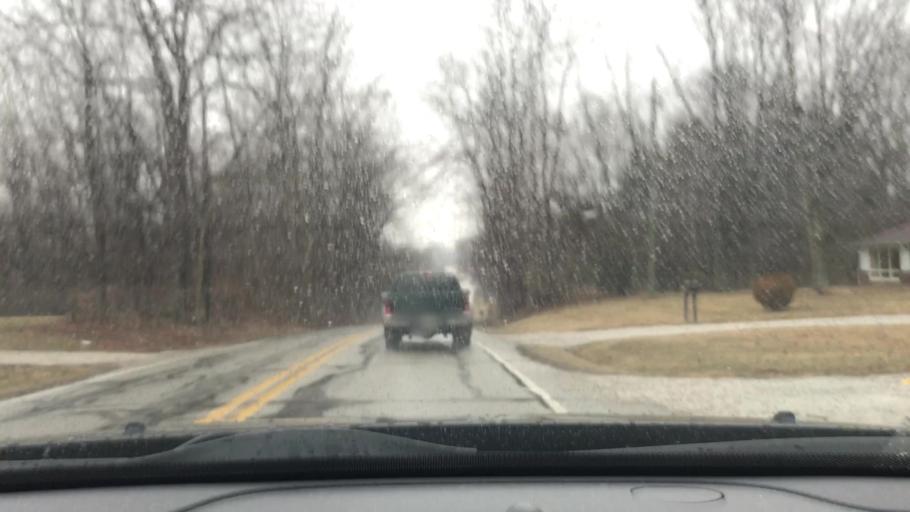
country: US
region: Indiana
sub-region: Morgan County
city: Mooresville
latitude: 39.5915
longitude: -86.3375
